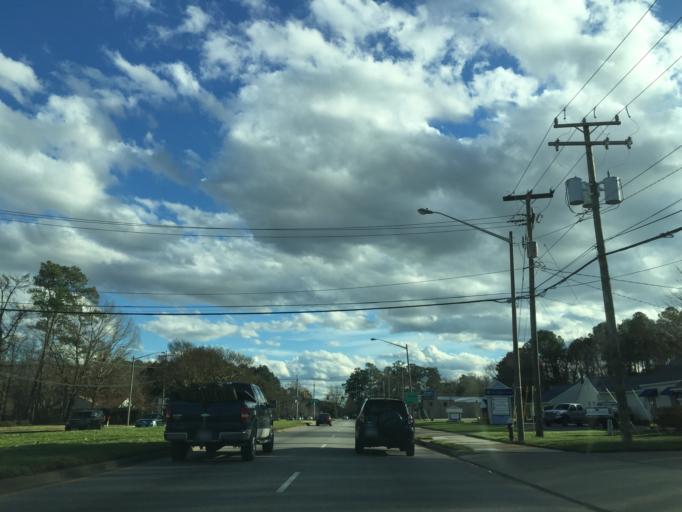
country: US
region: Virginia
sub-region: York County
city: Yorktown
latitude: 37.1119
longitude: -76.5179
